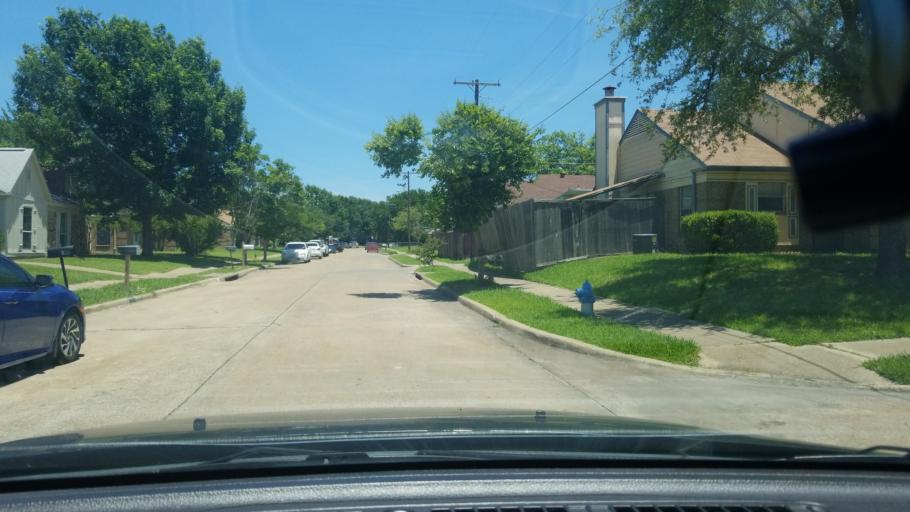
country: US
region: Texas
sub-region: Dallas County
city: Mesquite
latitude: 32.7738
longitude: -96.6079
